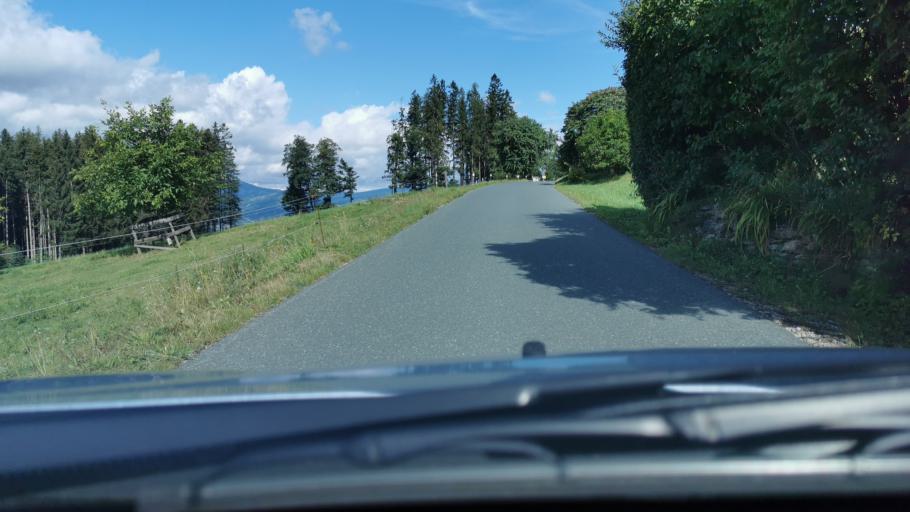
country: AT
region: Styria
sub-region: Politischer Bezirk Weiz
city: Koglhof
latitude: 47.3111
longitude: 15.7059
